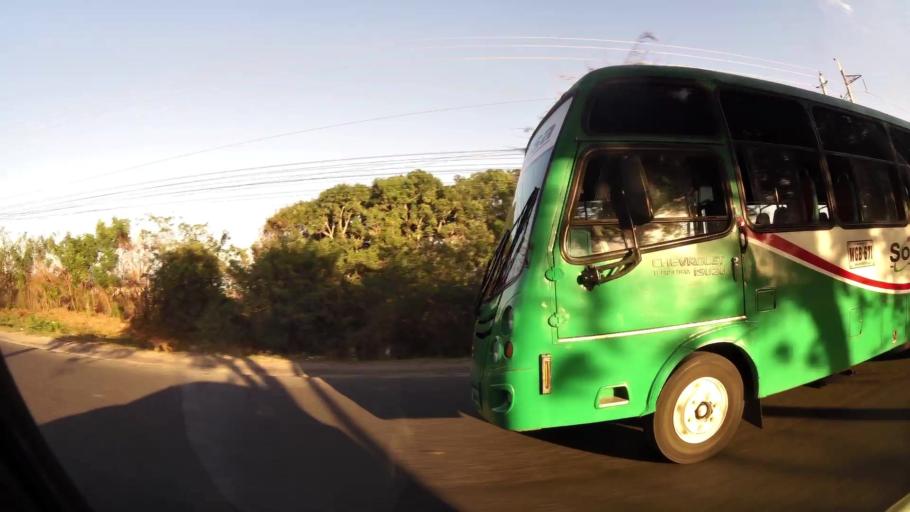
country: CO
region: Atlantico
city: Soledad
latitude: 10.8961
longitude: -74.8036
